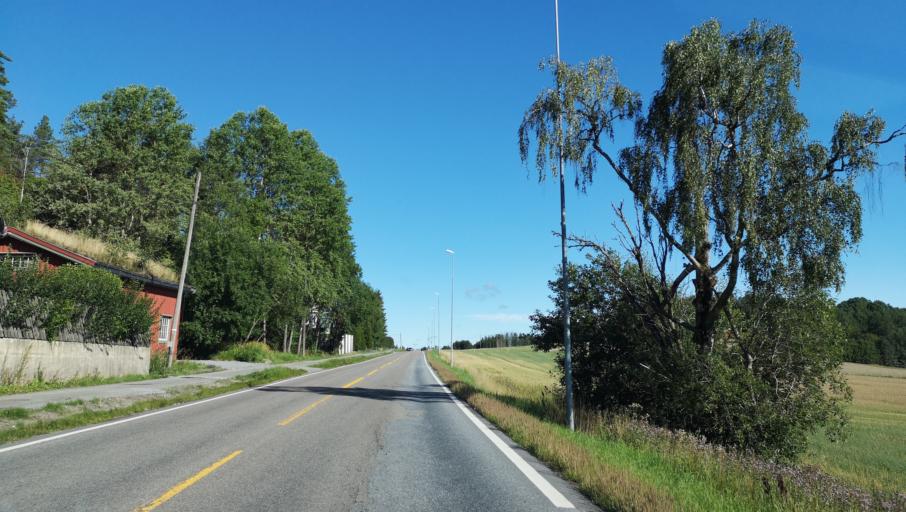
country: NO
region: Ostfold
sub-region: Spydeberg
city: Spydeberg
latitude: 59.5906
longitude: 11.1114
